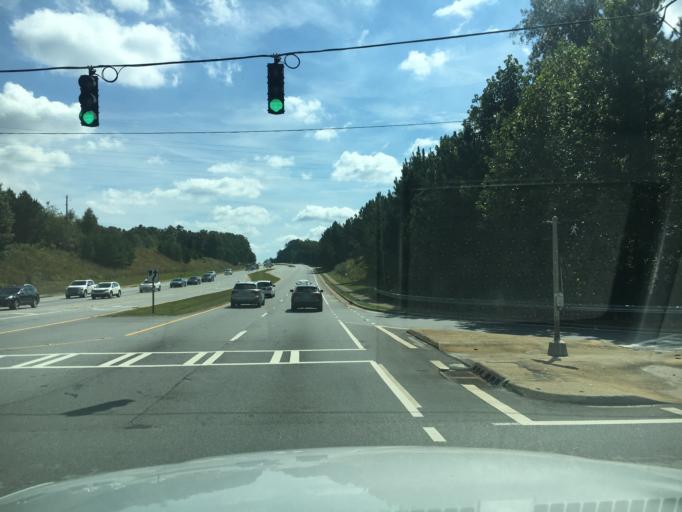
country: US
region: Georgia
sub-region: Gwinnett County
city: Duluth
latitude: 34.0199
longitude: -84.1174
